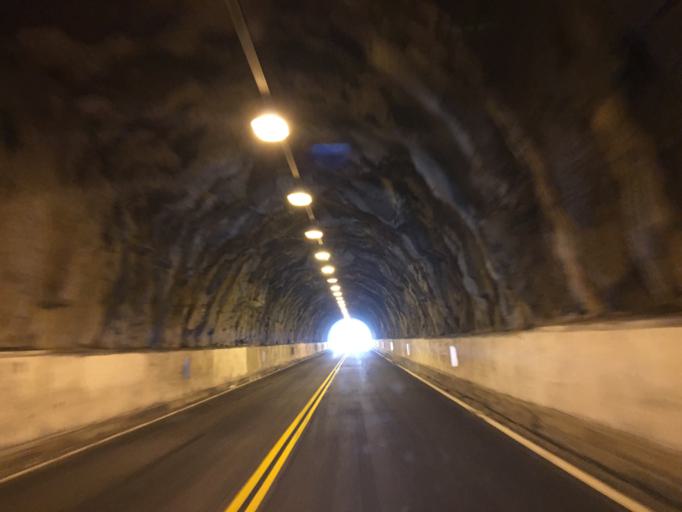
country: US
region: California
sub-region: San Bernardino County
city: San Antonio Heights
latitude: 34.2011
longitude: -117.6760
